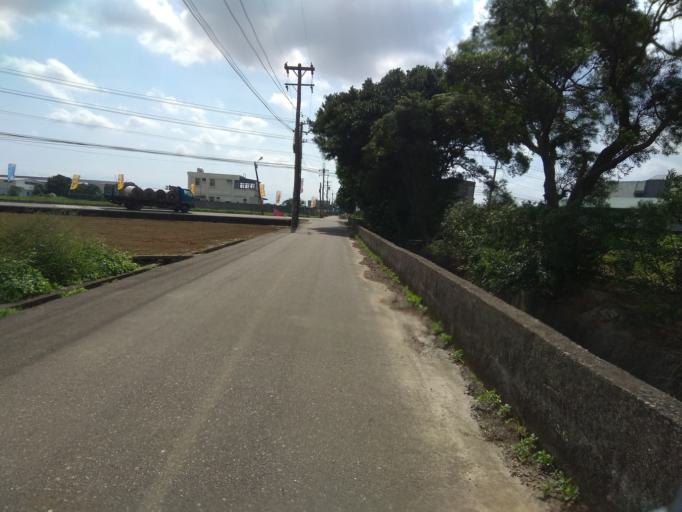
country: TW
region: Taiwan
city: Taoyuan City
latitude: 25.0732
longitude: 121.2489
